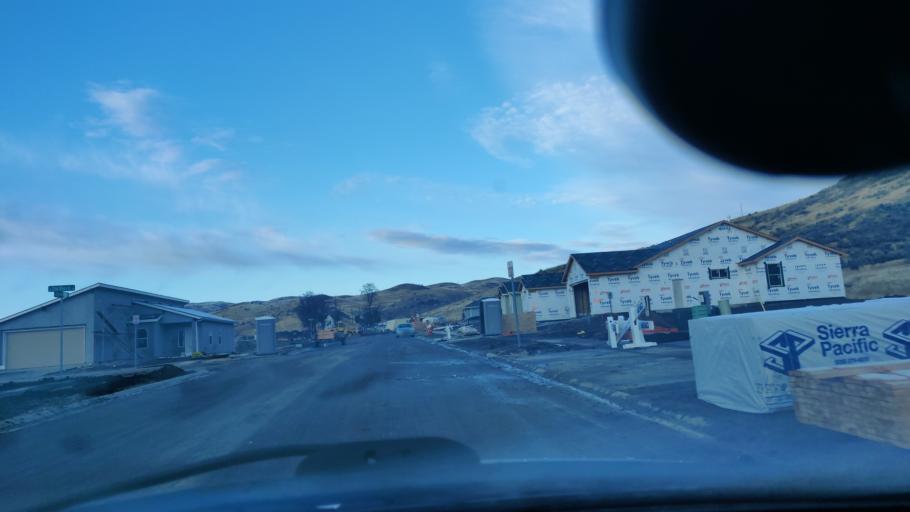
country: US
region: Idaho
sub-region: Ada County
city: Eagle
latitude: 43.7909
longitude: -116.2596
